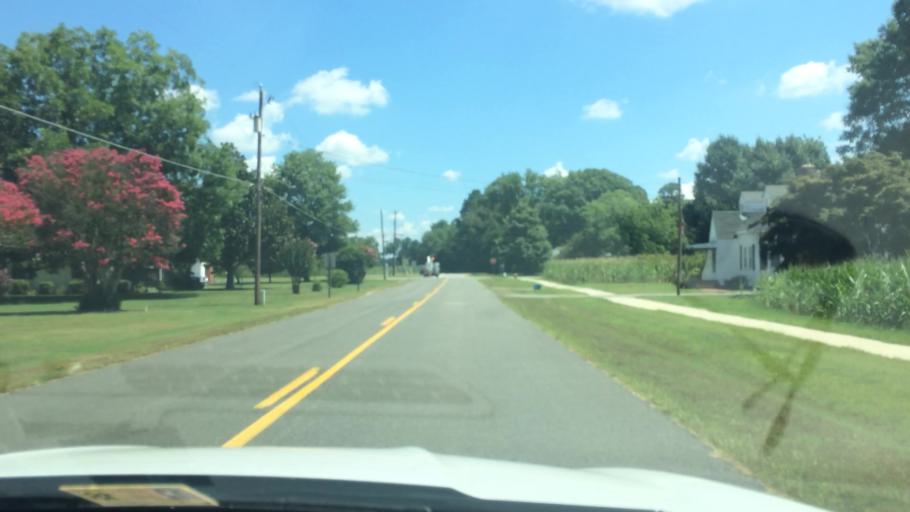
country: US
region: Virginia
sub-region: King William County
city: West Point
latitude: 37.5653
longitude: -76.8032
